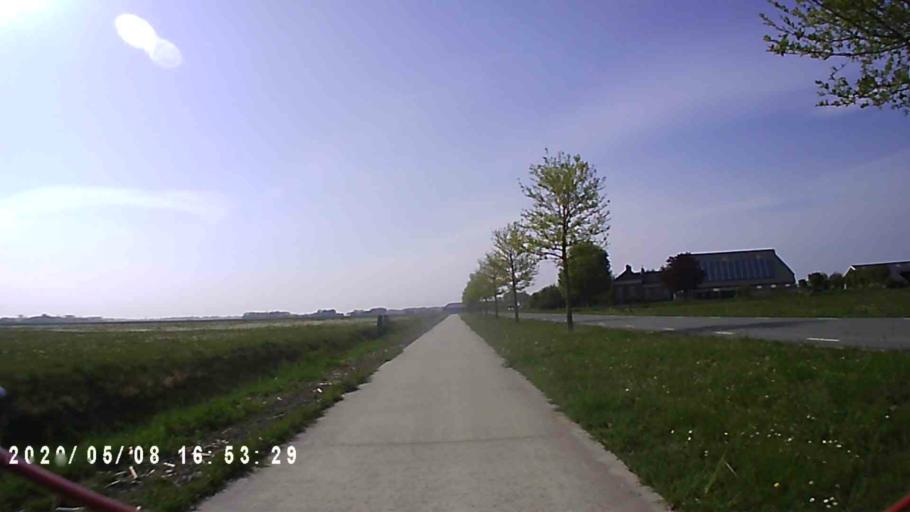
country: NL
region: Groningen
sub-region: Gemeente Bedum
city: Bedum
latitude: 53.3869
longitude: 6.6249
